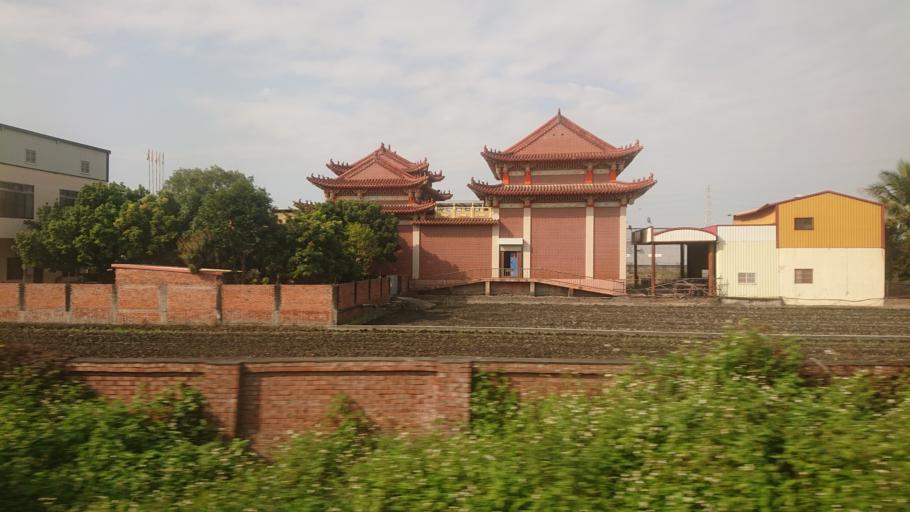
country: TW
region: Taiwan
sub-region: Nantou
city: Nantou
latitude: 23.9141
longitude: 120.5759
